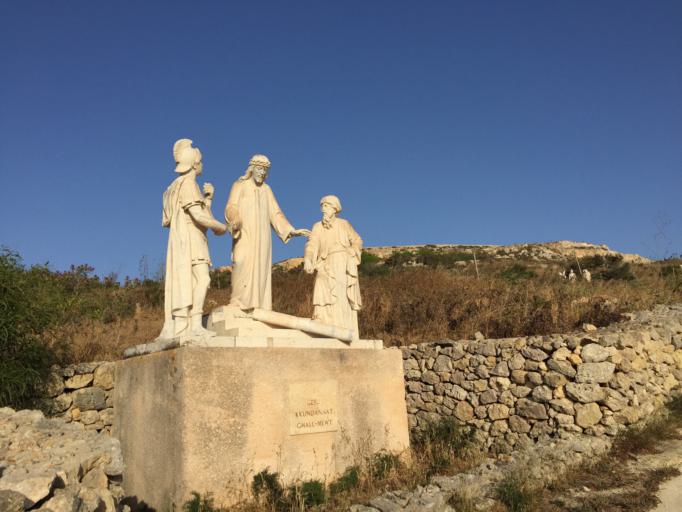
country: MT
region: L-Gharb
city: Gharb
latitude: 36.0606
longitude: 14.2175
